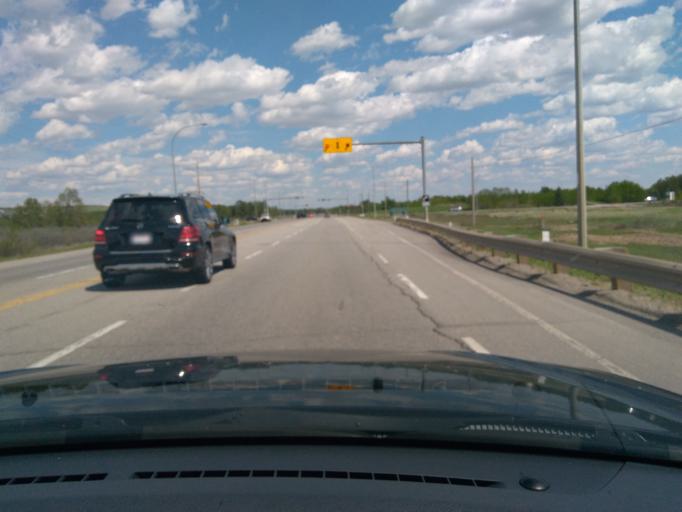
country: CA
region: Alberta
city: Calgary
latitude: 51.0162
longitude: -114.2648
